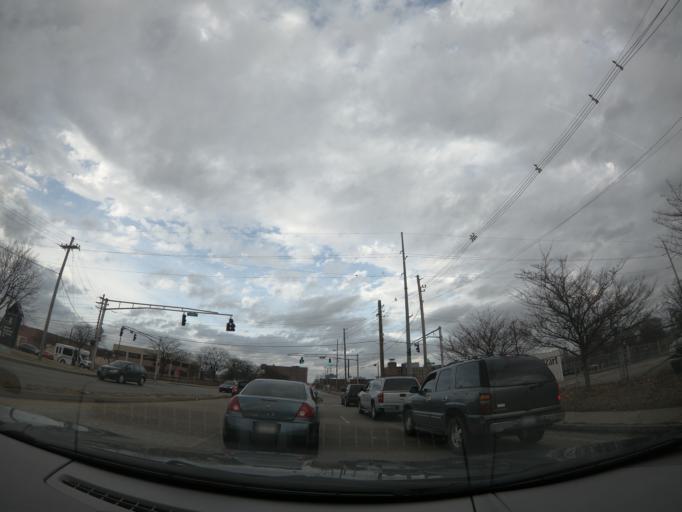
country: US
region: Kentucky
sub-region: Jefferson County
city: Louisville
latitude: 38.2400
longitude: -85.7679
